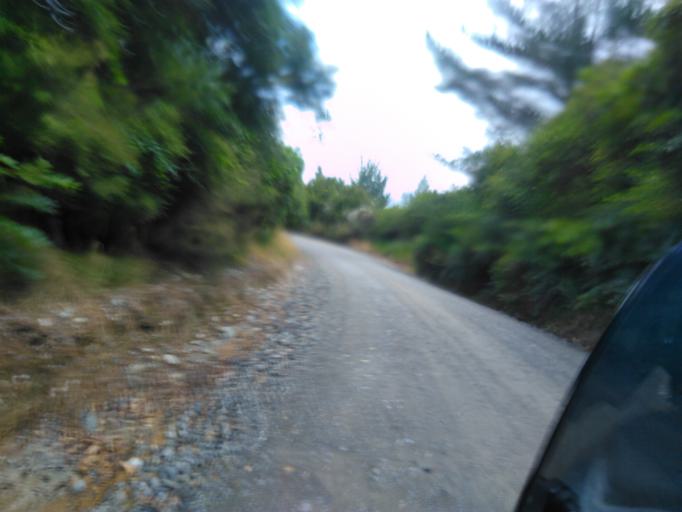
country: NZ
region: Gisborne
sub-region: Gisborne District
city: Gisborne
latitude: -38.2366
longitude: 178.0695
